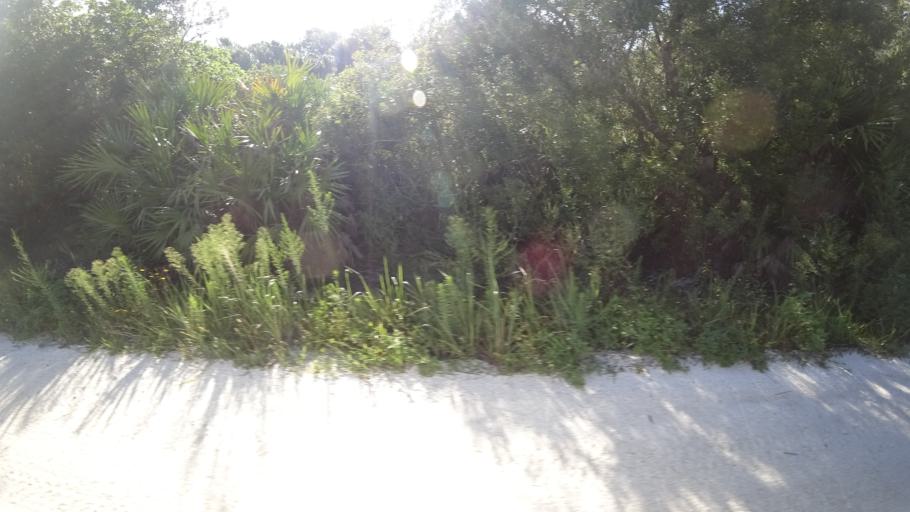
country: US
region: Florida
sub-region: Sarasota County
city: The Meadows
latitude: 27.4201
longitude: -82.2614
